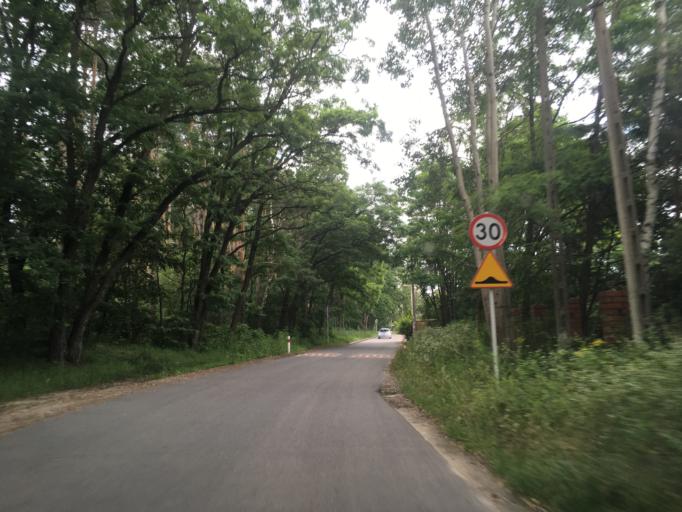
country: PL
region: Masovian Voivodeship
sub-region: Powiat piaseczynski
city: Lesznowola
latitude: 52.0769
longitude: 20.9461
